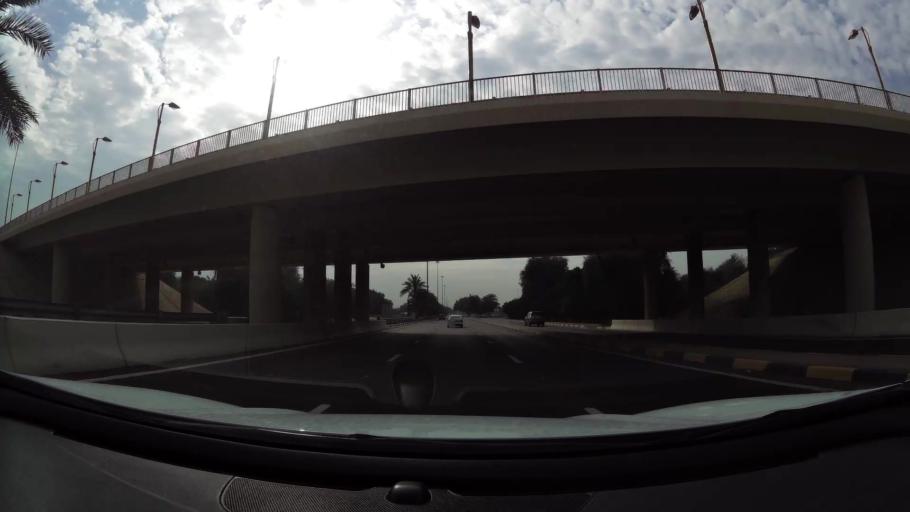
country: AE
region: Abu Dhabi
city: Al Ain
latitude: 24.1845
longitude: 55.5961
